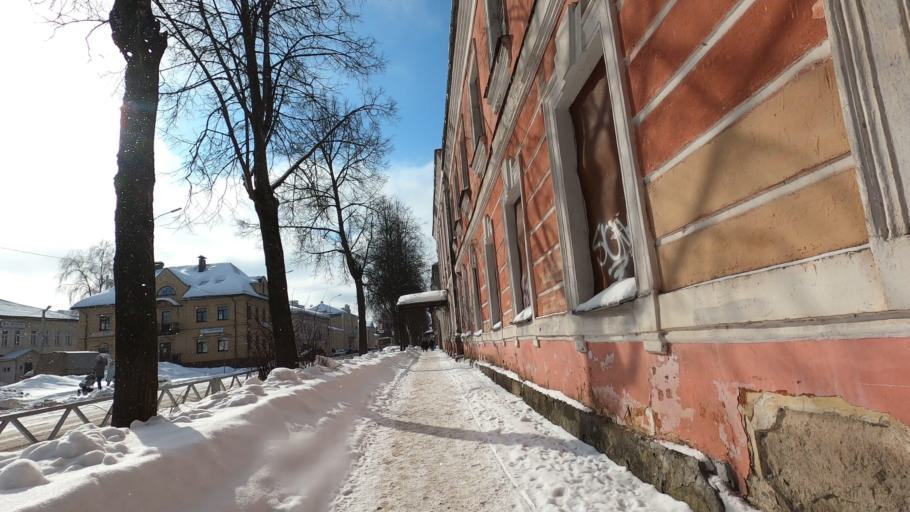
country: RU
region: Jaroslavl
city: Rybinsk
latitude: 58.0480
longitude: 38.8490
